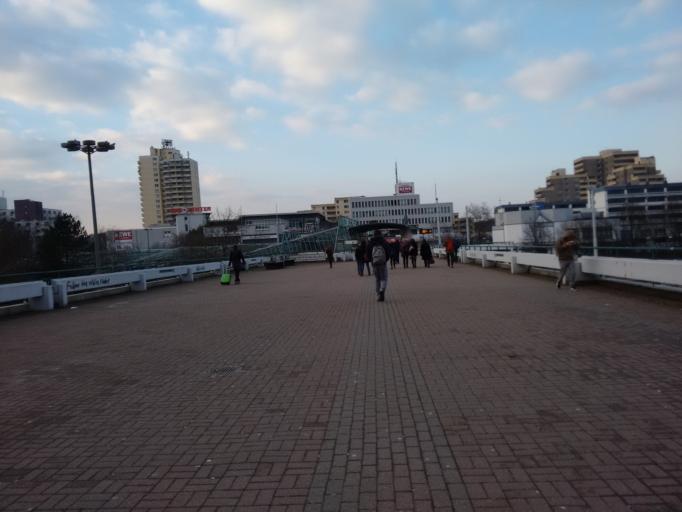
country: DE
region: North Rhine-Westphalia
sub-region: Regierungsbezirk Arnsberg
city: Bochum
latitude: 51.4465
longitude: 7.2599
